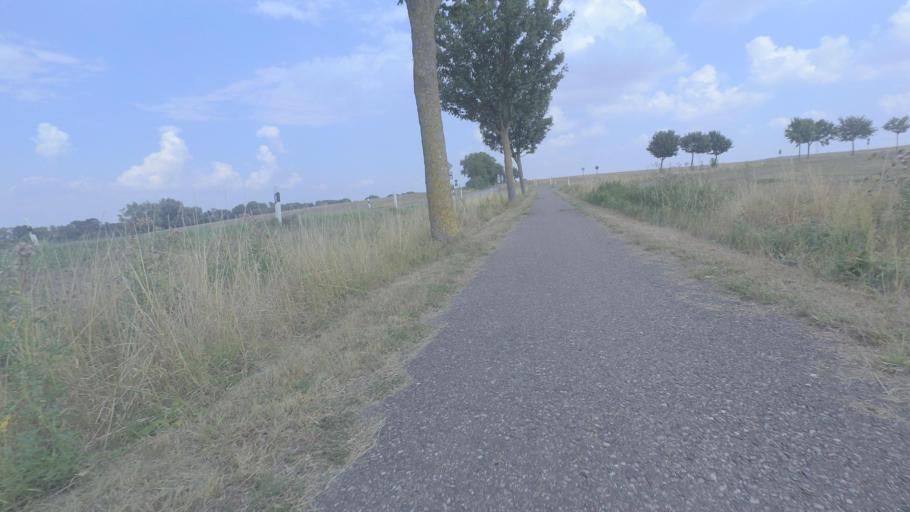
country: DE
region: Mecklenburg-Vorpommern
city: Neukalen
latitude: 53.7721
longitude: 12.8559
